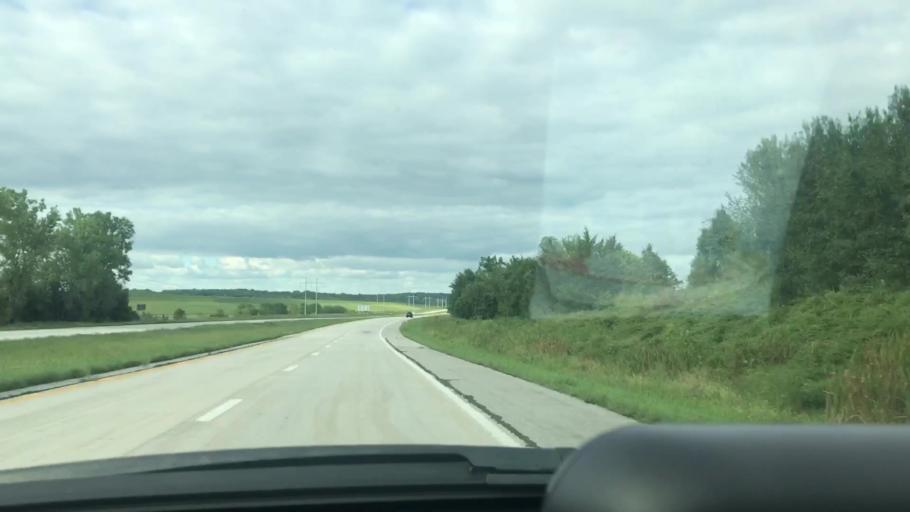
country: US
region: Missouri
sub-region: Benton County
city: Warsaw
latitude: 38.2805
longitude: -93.3628
